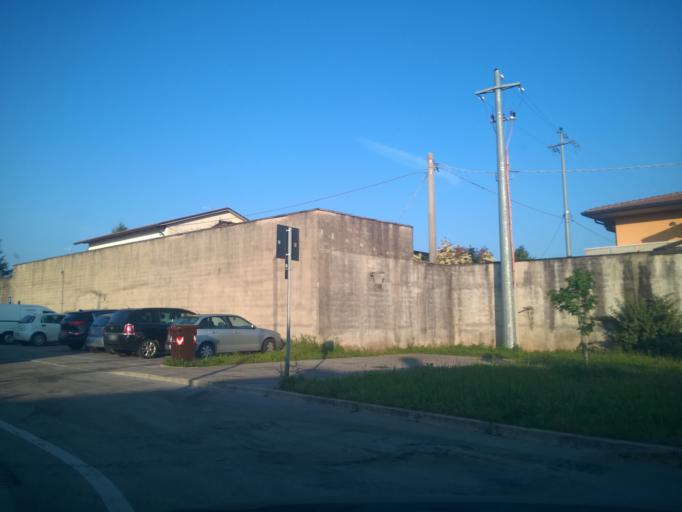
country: IT
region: Veneto
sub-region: Provincia di Vicenza
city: Zane
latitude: 45.7212
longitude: 11.4551
